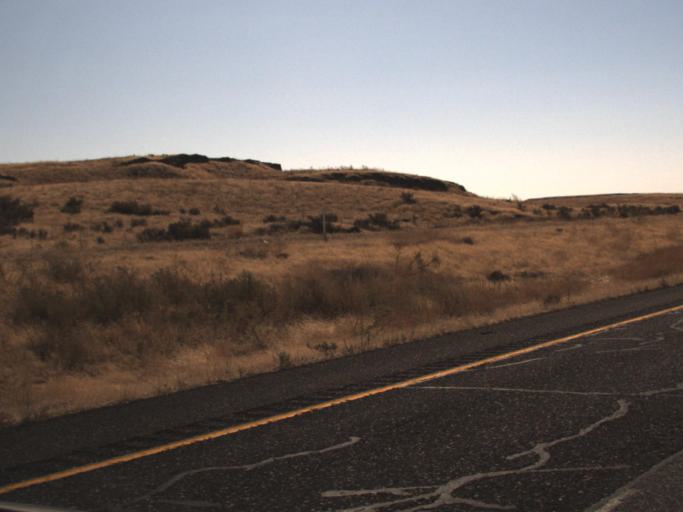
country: US
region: Washington
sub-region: Franklin County
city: Basin City
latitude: 46.5017
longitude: -119.0151
